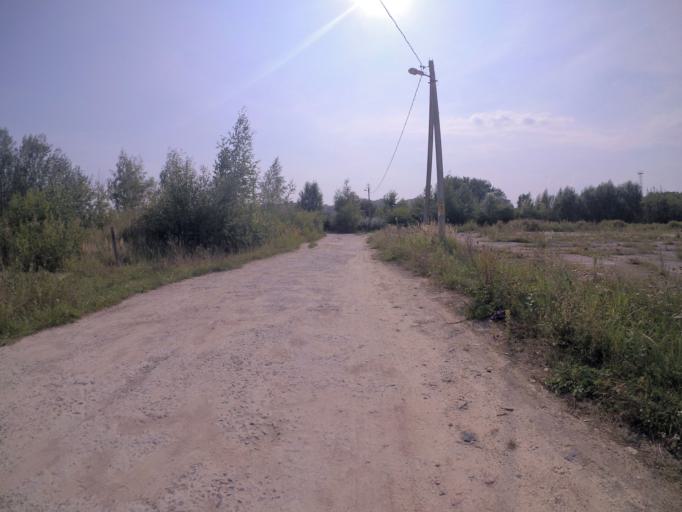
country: BY
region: Grodnenskaya
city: Hrodna
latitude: 53.7190
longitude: 23.8465
